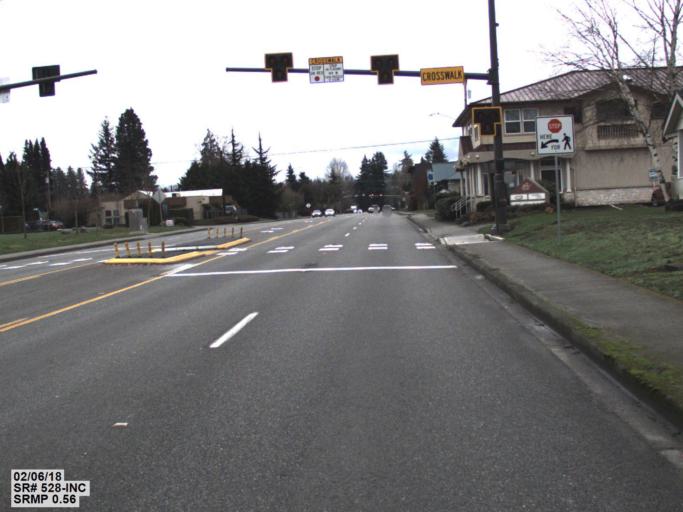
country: US
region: Washington
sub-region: Snohomish County
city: Marysville
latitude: 48.0518
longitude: -122.1728
